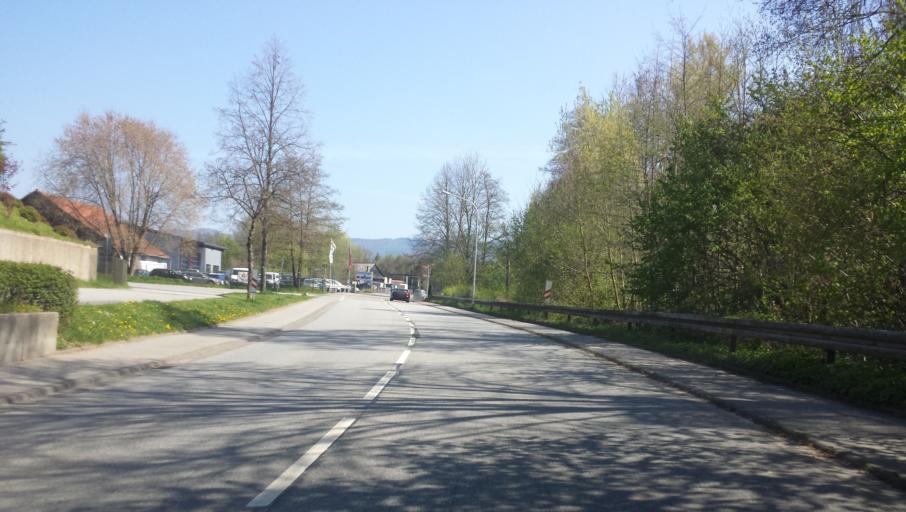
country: DE
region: Hesse
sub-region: Regierungsbezirk Darmstadt
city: Morlenbach
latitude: 49.5984
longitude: 8.7296
